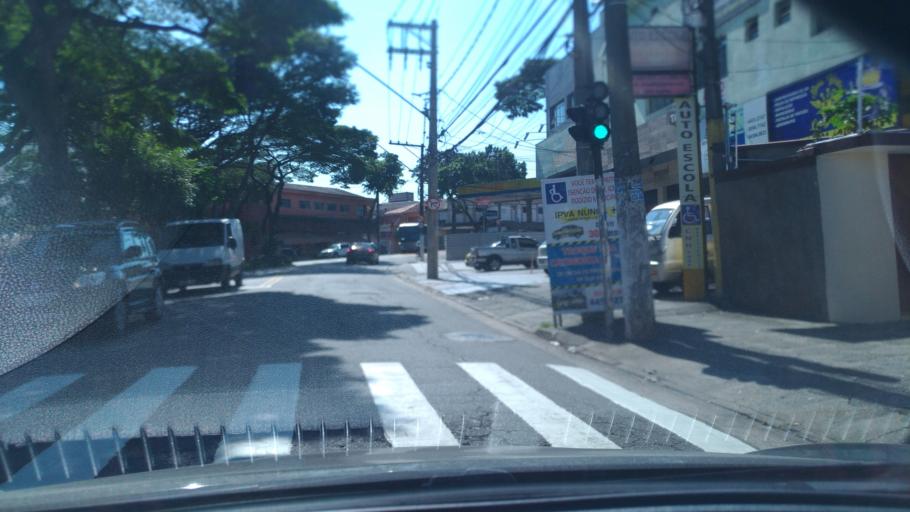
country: BR
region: Sao Paulo
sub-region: Santo Andre
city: Santo Andre
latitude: -23.6657
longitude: -46.5425
